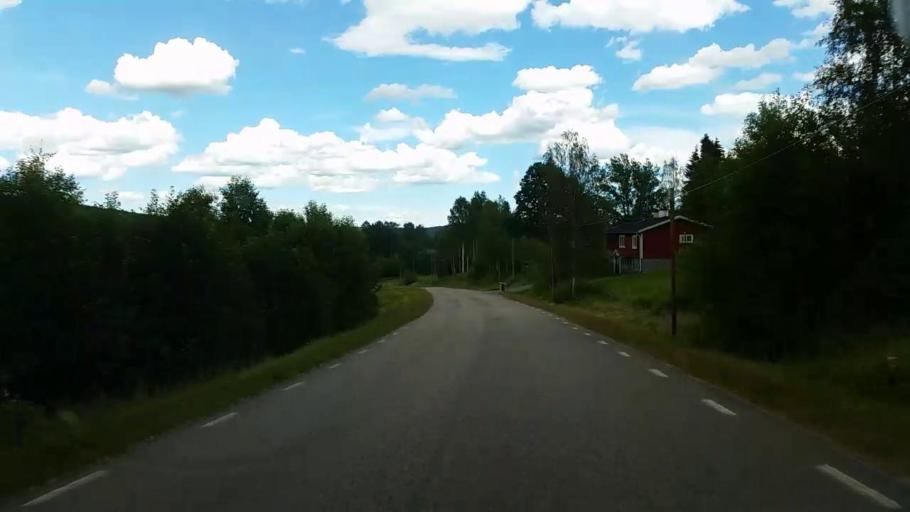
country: SE
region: Gaevleborg
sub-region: Ljusdals Kommun
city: Jaervsoe
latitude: 61.6673
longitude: 16.0879
